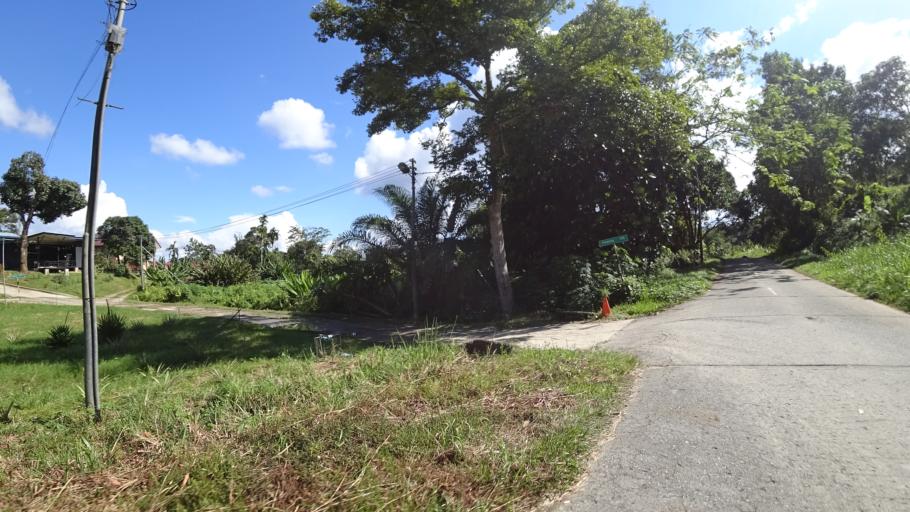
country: BN
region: Tutong
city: Tutong
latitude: 4.7378
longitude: 114.7910
